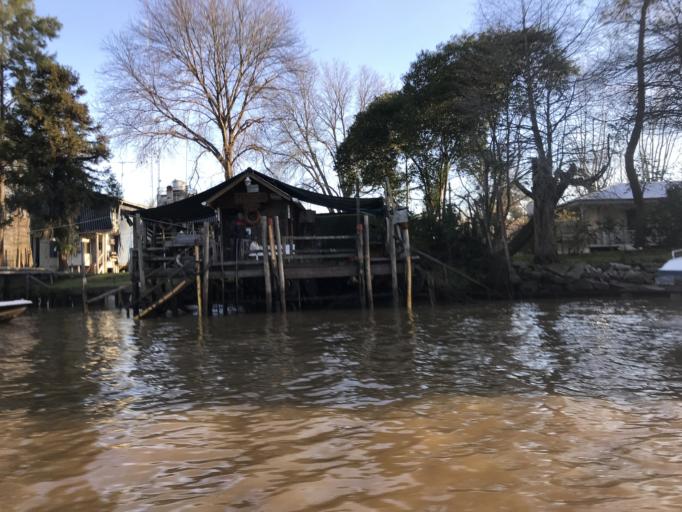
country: AR
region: Buenos Aires
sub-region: Partido de Tigre
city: Tigre
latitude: -34.3716
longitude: -58.5905
